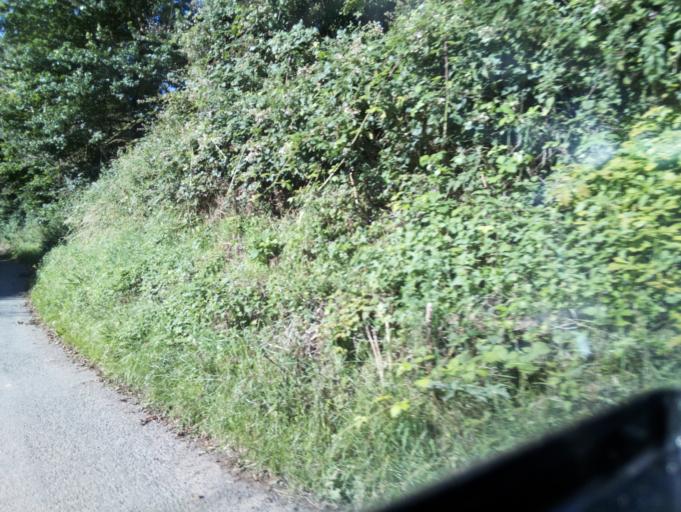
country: GB
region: England
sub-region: Herefordshire
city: Ross on Wye
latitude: 51.9451
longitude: -2.5733
